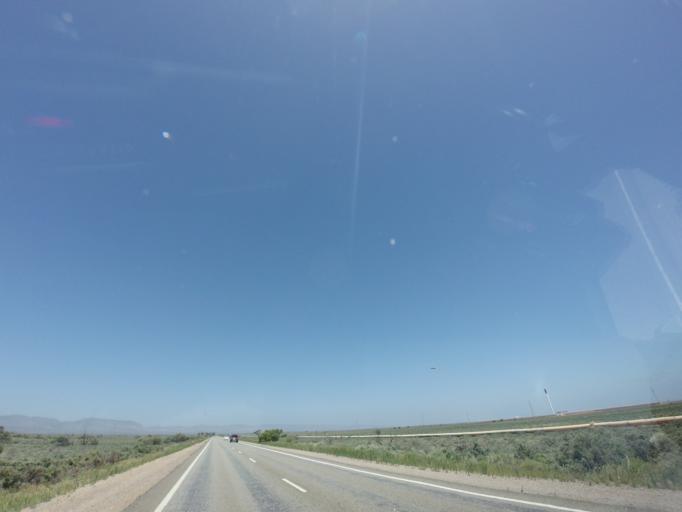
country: AU
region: South Australia
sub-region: Port Augusta
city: Port Augusta
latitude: -32.5343
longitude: 137.8435
